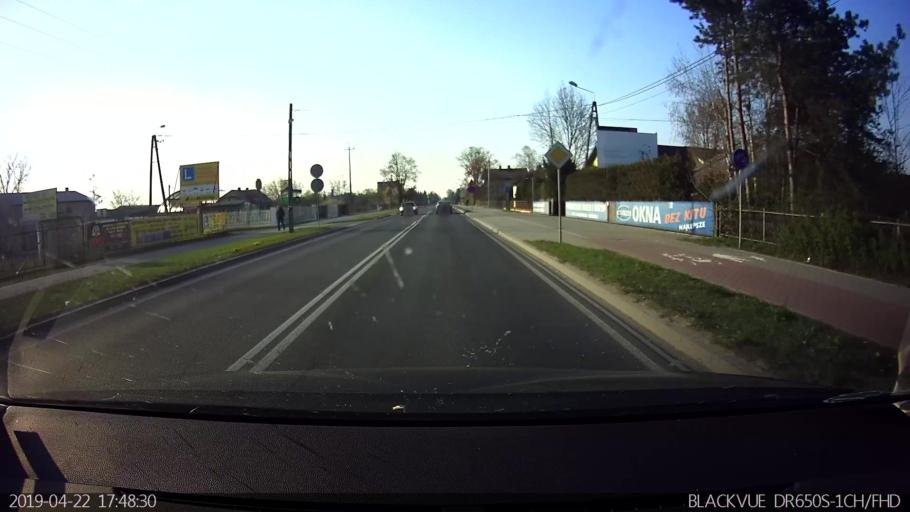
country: PL
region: Masovian Voivodeship
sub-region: Powiat wegrowski
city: Wegrow
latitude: 52.4055
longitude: 22.0142
